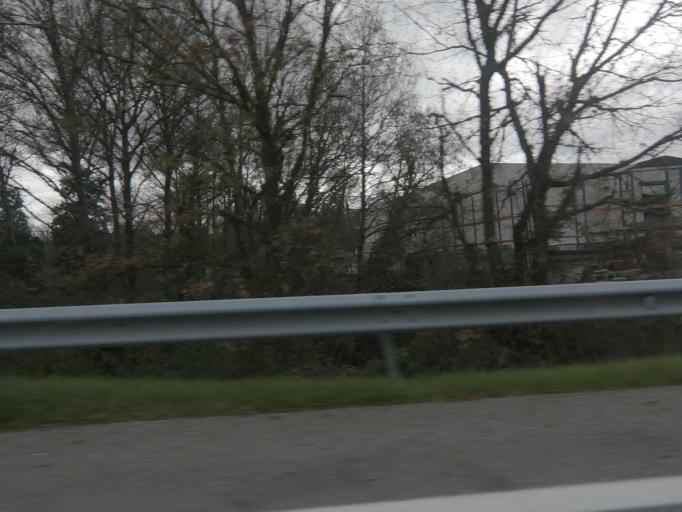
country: ES
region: Galicia
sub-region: Provincia de Ourense
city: Allariz
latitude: 42.1977
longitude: -7.8009
